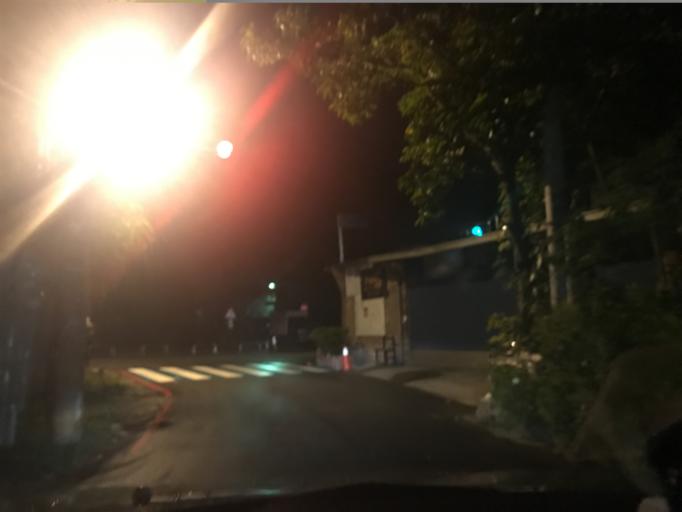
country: TW
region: Taiwan
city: Daxi
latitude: 24.8560
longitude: 121.2181
